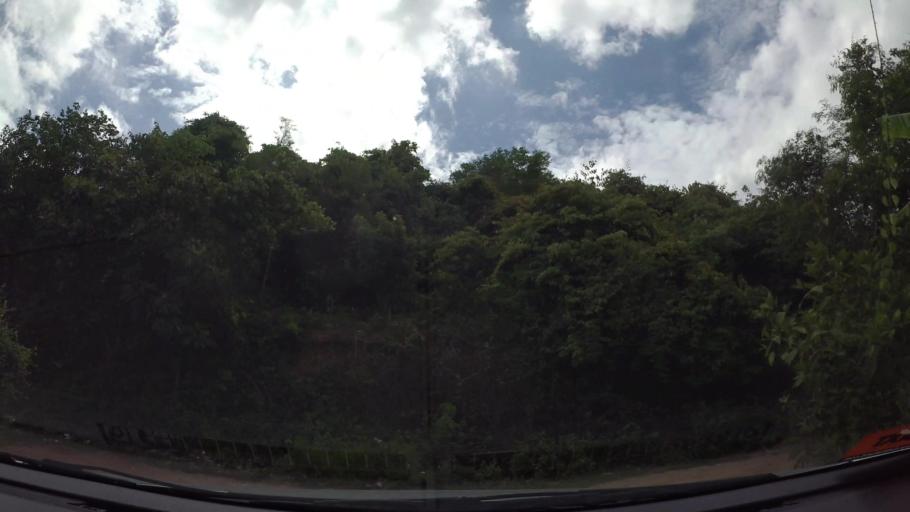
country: TH
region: Chon Buri
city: Sattahip
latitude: 12.6941
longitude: 100.9059
